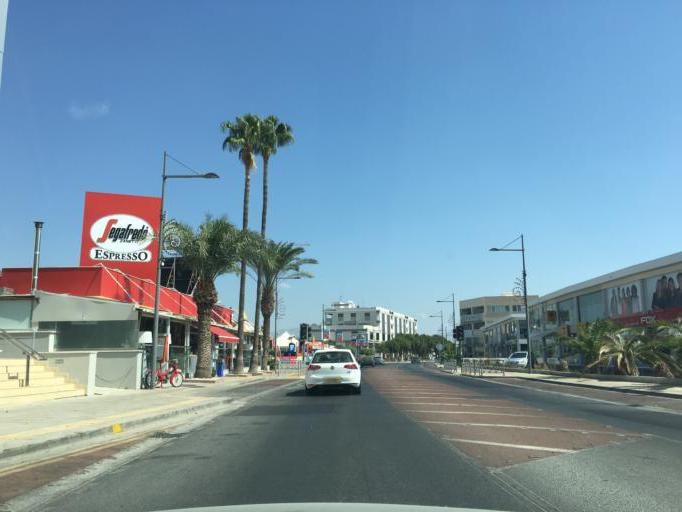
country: CY
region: Lefkosia
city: Nicosia
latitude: 35.1631
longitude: 33.3176
